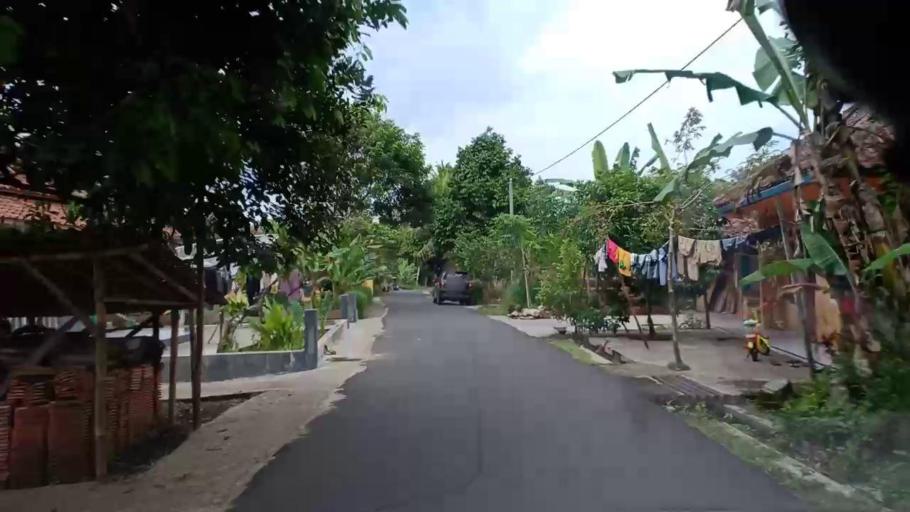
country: ID
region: West Java
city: Gerempay
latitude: -7.3378
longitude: 108.2980
